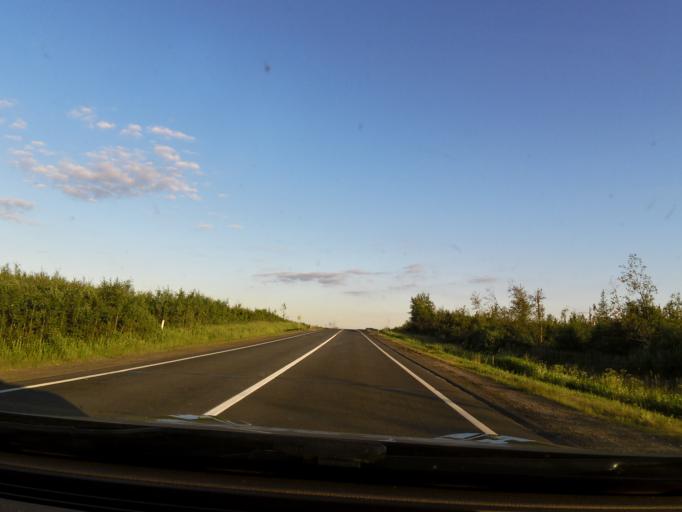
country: RU
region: Jaroslavl
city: Prechistoye
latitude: 58.5910
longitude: 40.3457
